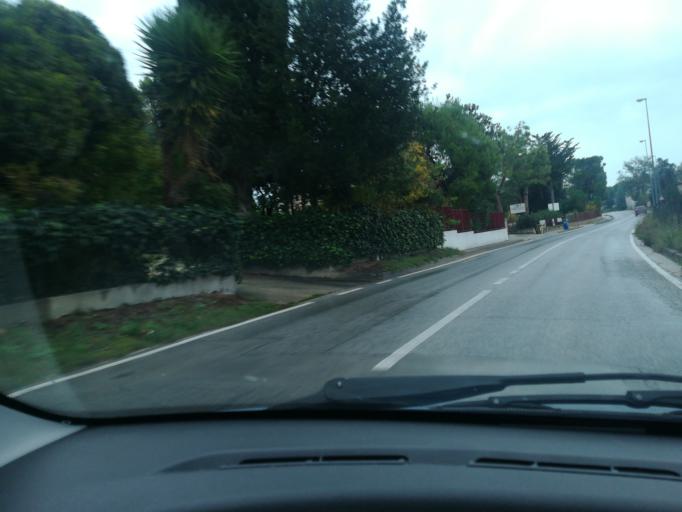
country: IT
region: The Marches
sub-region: Provincia di Macerata
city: Santa Maria Apparente
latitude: 43.2965
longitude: 13.6854
